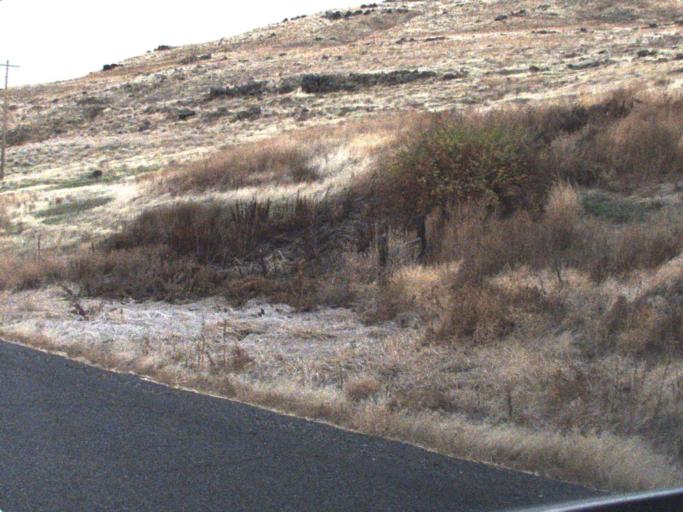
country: US
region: Washington
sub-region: Columbia County
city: Dayton
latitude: 46.7772
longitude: -118.0648
